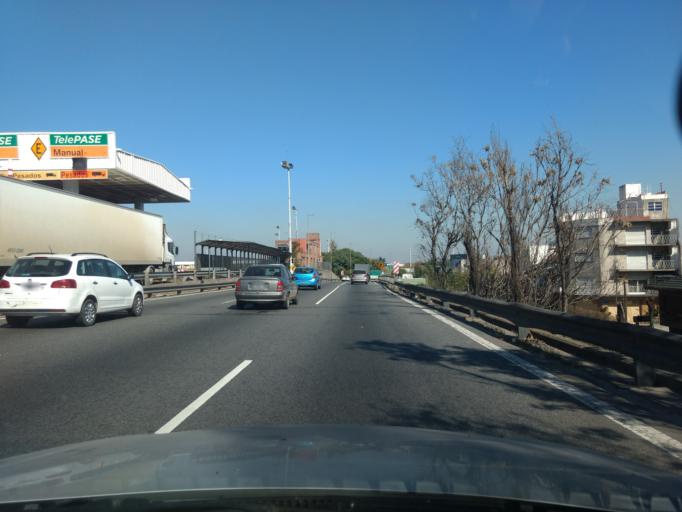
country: AR
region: Buenos Aires F.D.
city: Villa Lugano
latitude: -34.6475
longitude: -58.4643
